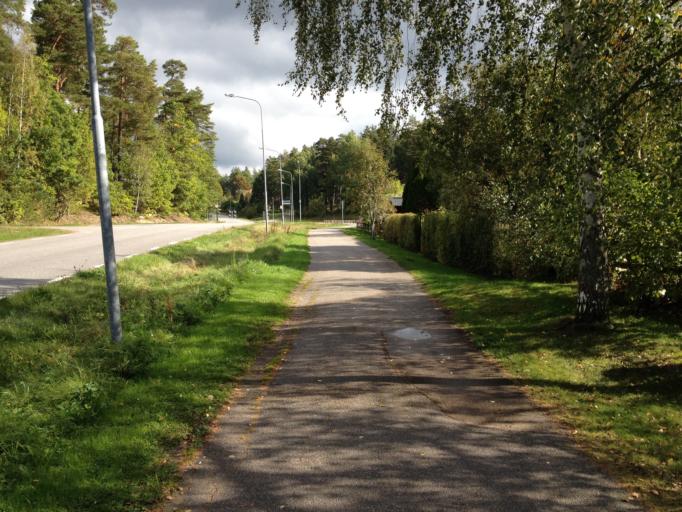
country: SE
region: OEstergoetland
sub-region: Linkopings Kommun
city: Sturefors
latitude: 58.3056
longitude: 15.8691
